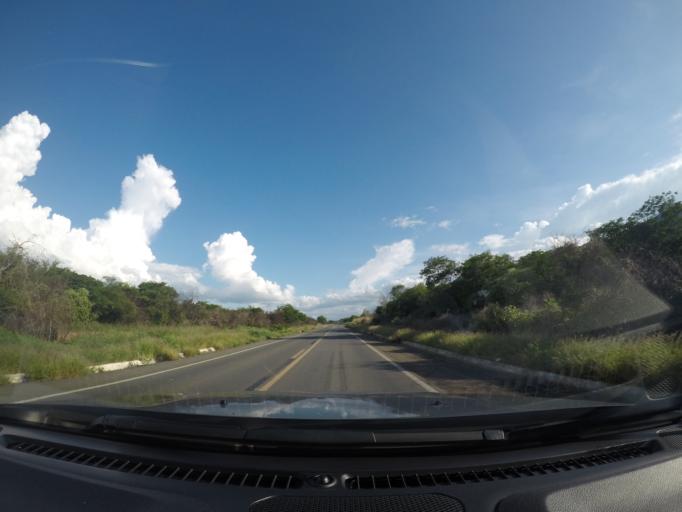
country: BR
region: Bahia
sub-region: Oliveira Dos Brejinhos
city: Oliveira dos Brejinhos
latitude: -12.0539
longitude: -42.9663
